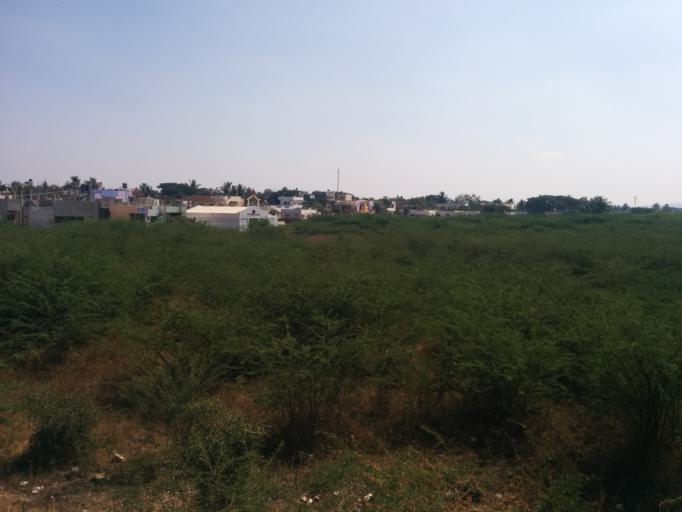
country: IN
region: Karnataka
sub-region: Gadag
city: Gadag
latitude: 15.4373
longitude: 75.6496
